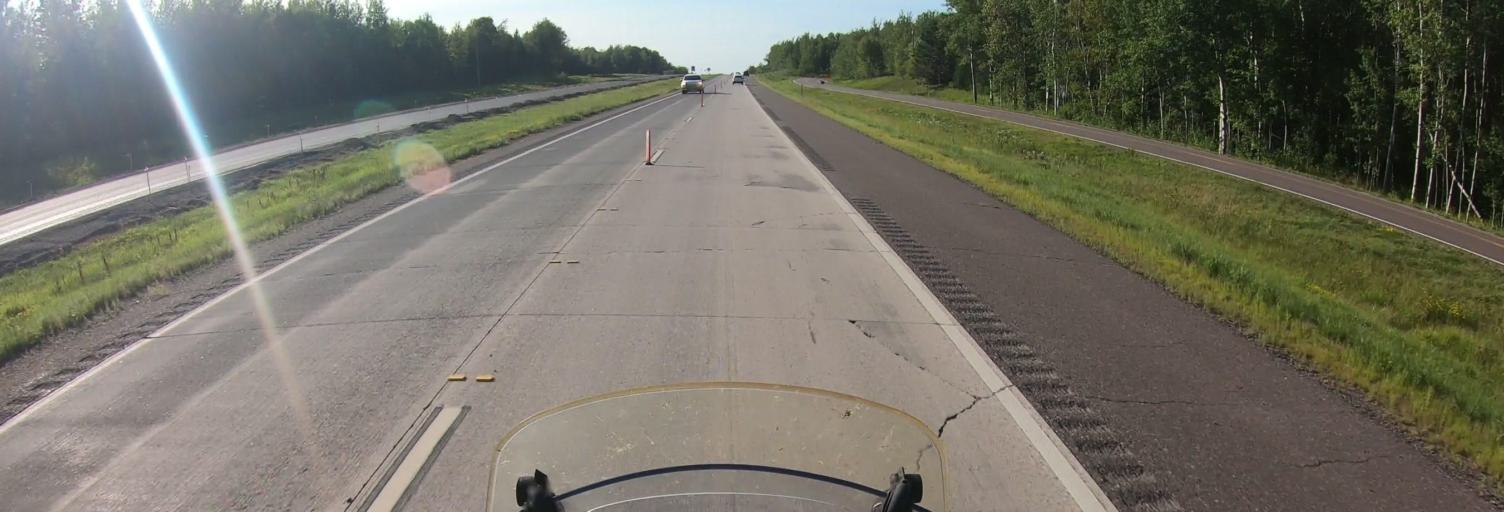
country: US
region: Minnesota
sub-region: Saint Louis County
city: Hermantown
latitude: 46.8990
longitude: -92.3716
